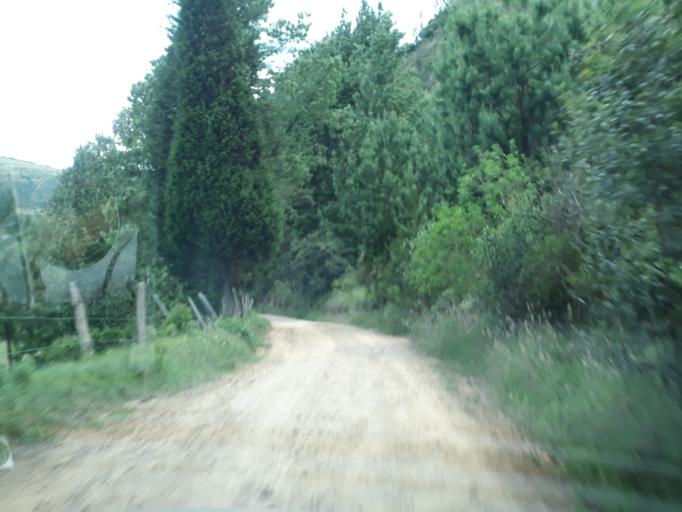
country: CO
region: Boyaca
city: Santa Rosa de Viterbo
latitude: 5.8661
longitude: -72.9676
